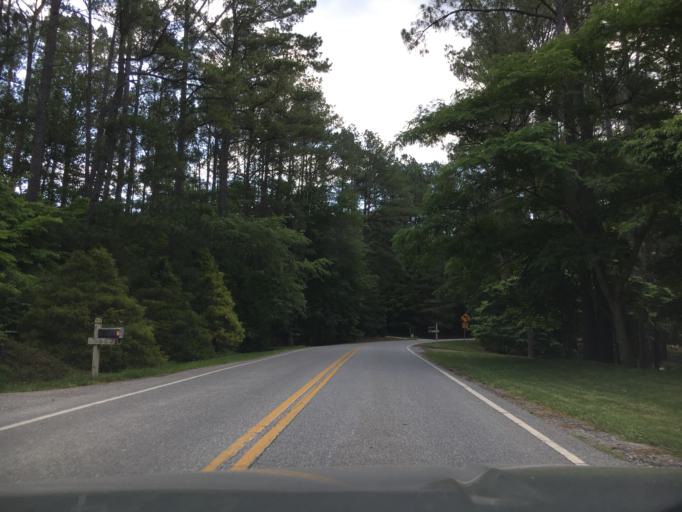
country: US
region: Virginia
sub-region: Bedford County
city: Forest
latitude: 37.3865
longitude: -79.2556
